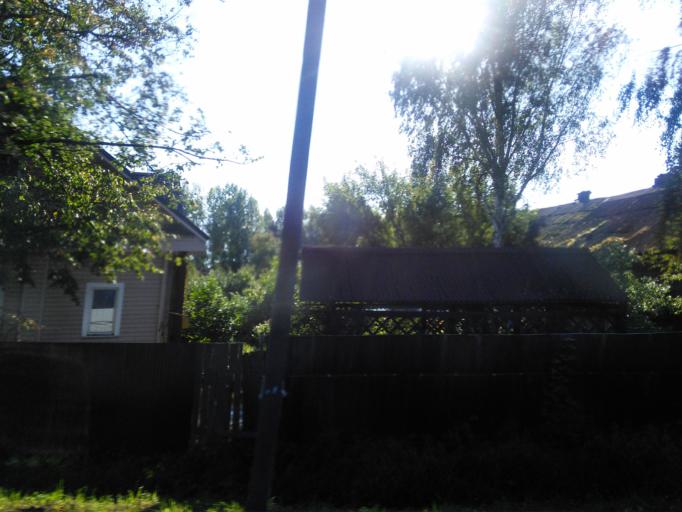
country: RU
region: Jaroslavl
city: Rybinsk
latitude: 58.0575
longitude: 38.8550
